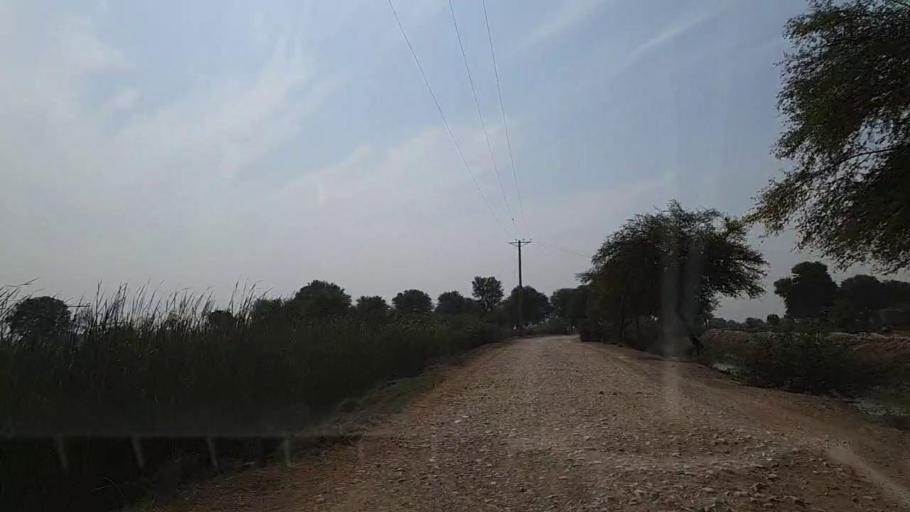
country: PK
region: Sindh
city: Mirpur Batoro
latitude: 24.6160
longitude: 68.2369
